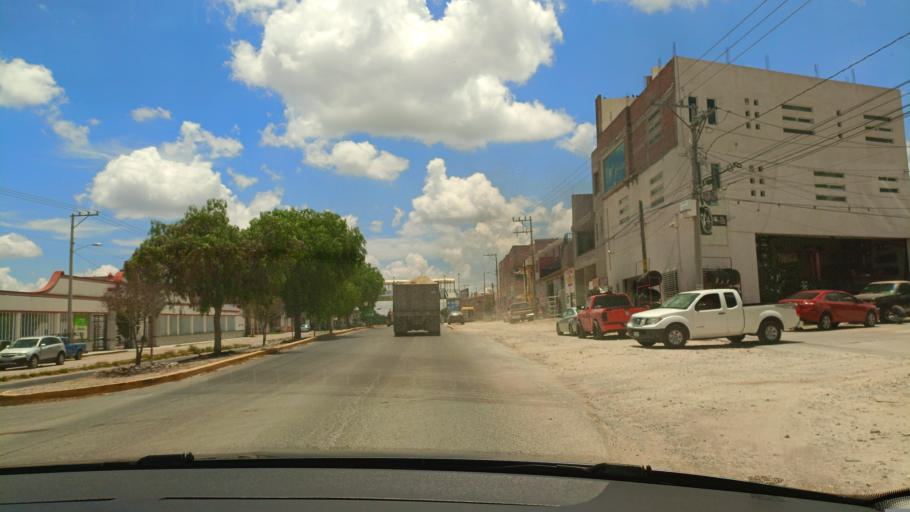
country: MX
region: Guerrero
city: San Luis de la Paz
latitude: 21.2885
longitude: -100.5124
